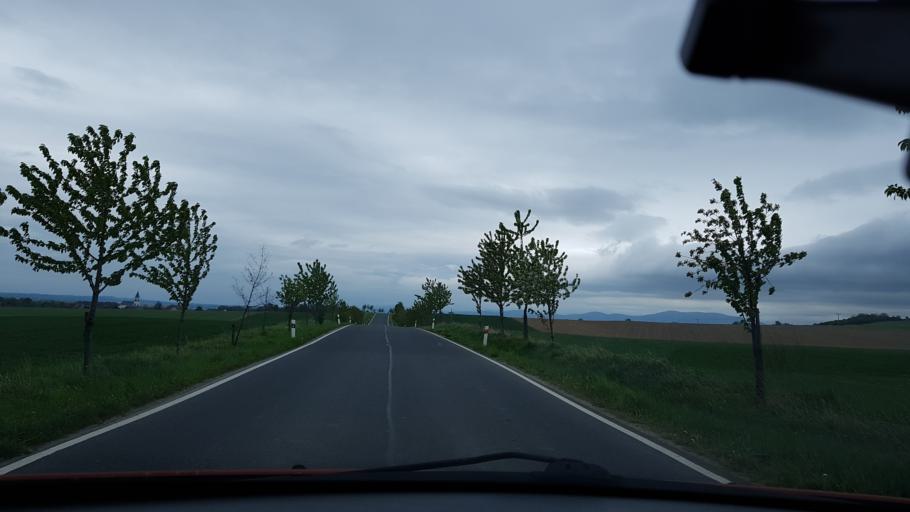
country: CZ
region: Olomoucky
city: Javornik
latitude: 50.4140
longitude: 16.9783
